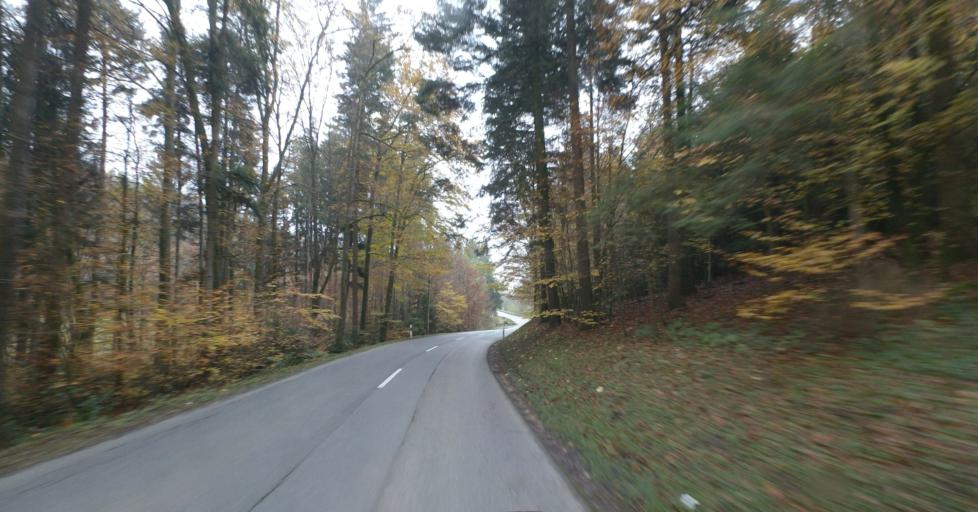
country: DE
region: Bavaria
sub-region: Upper Bavaria
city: Seeon-Seebruck
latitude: 47.9645
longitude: 12.5169
